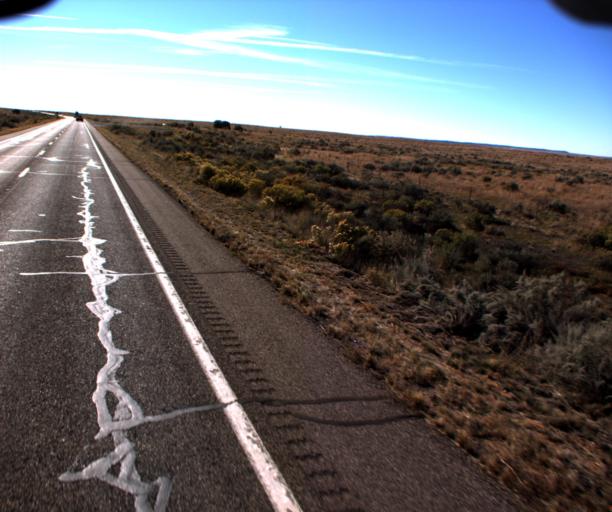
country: US
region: Arizona
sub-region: Mohave County
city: Colorado City
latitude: 36.8957
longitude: -112.9154
